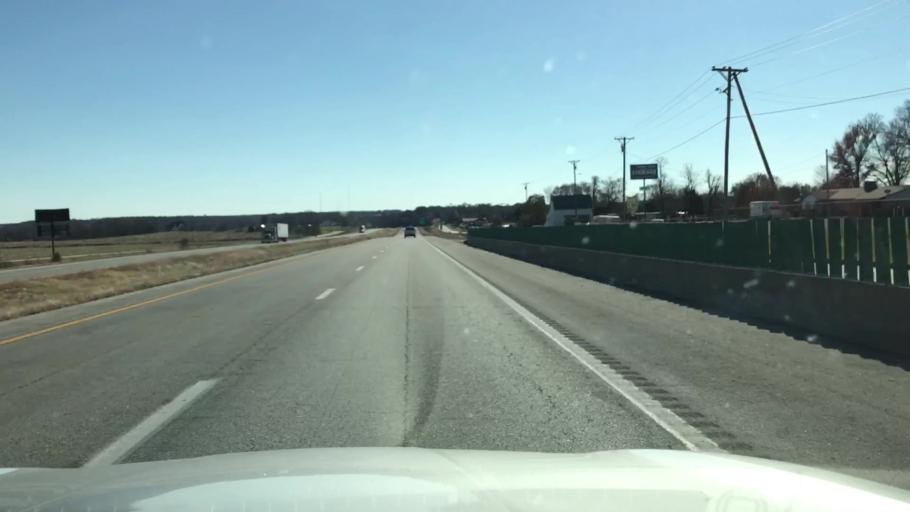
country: US
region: Missouri
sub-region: Jasper County
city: Carthage
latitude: 37.1231
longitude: -94.3111
